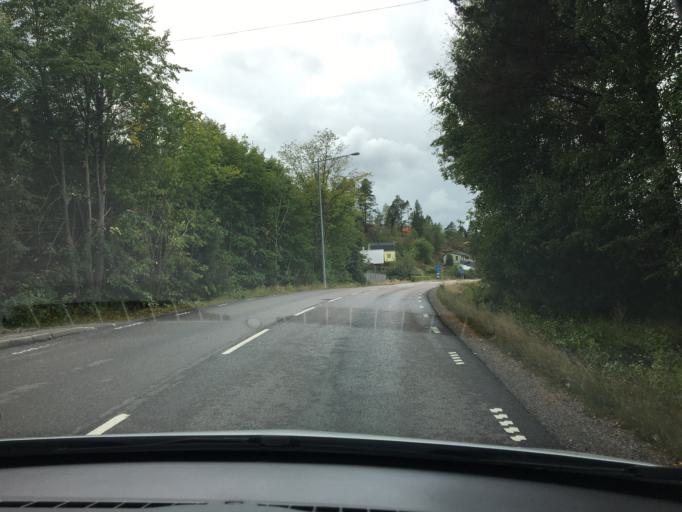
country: SE
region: Vaestra Goetaland
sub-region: Ale Kommun
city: Nodinge-Nol
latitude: 57.8842
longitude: 12.0831
